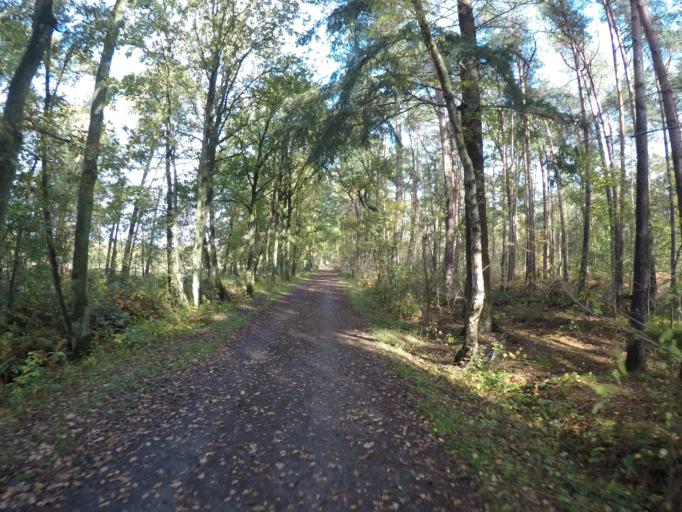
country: BE
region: Flanders
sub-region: Provincie Antwerpen
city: Zandhoven
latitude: 51.2555
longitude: 4.6706
